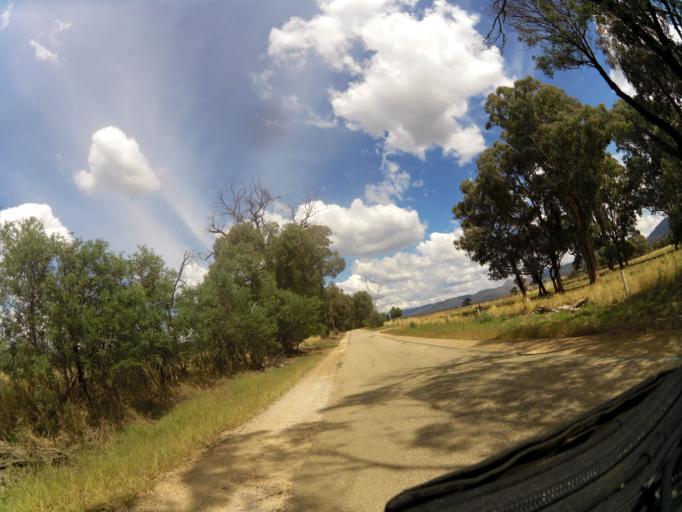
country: AU
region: Victoria
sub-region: Benalla
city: Benalla
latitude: -36.7607
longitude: 145.9772
